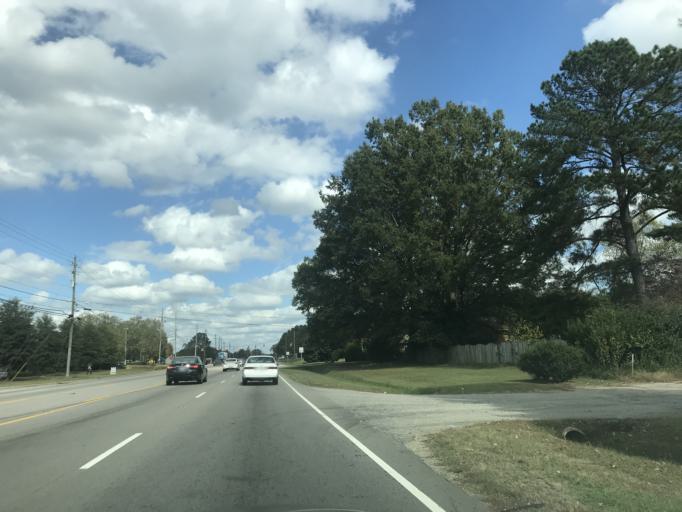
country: US
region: North Carolina
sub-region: Wake County
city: Garner
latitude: 35.7190
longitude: -78.6544
